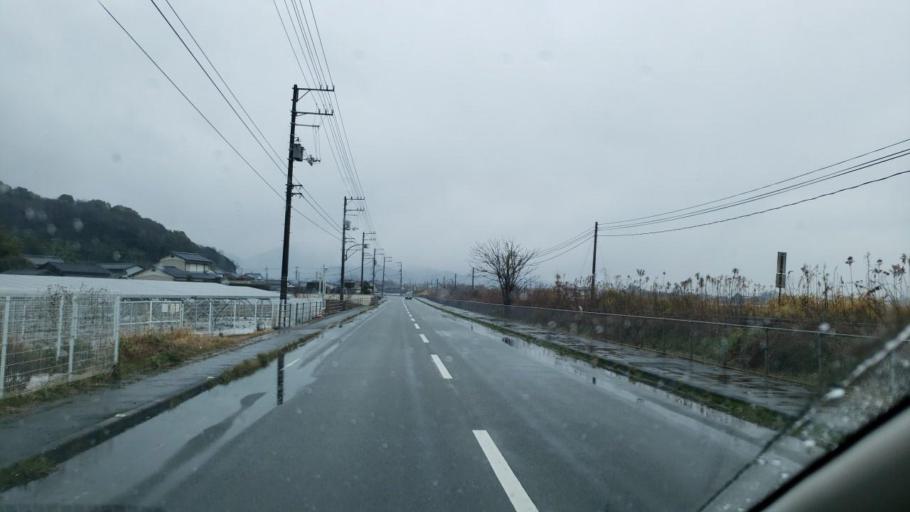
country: JP
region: Tokushima
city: Ishii
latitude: 34.1506
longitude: 134.4872
